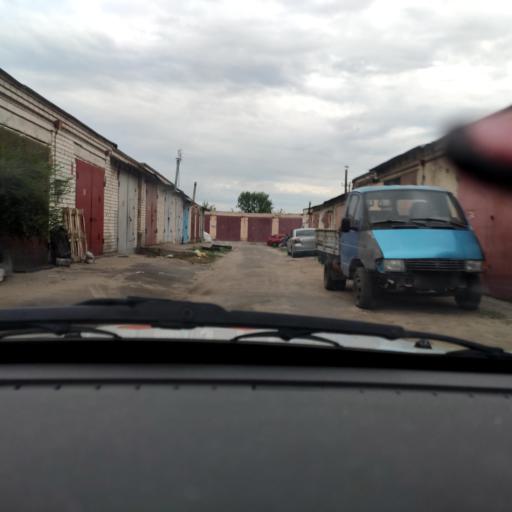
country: RU
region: Voronezj
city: Pridonskoy
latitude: 51.6400
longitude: 39.1188
